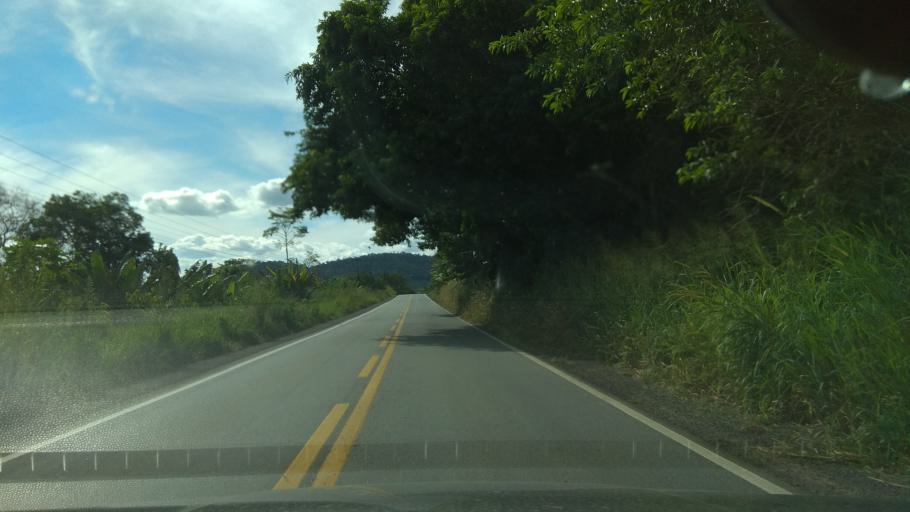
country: BR
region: Bahia
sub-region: Jitauna
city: Jitauna
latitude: -14.0305
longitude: -39.8318
